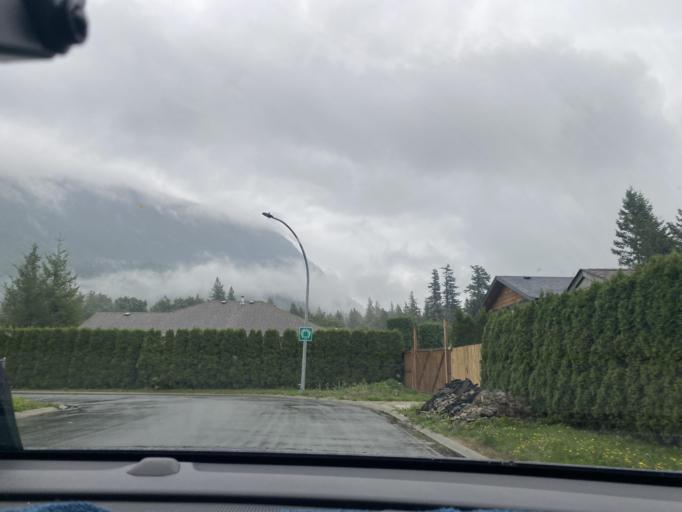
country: CA
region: British Columbia
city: Agassiz
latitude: 49.2867
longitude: -121.7803
